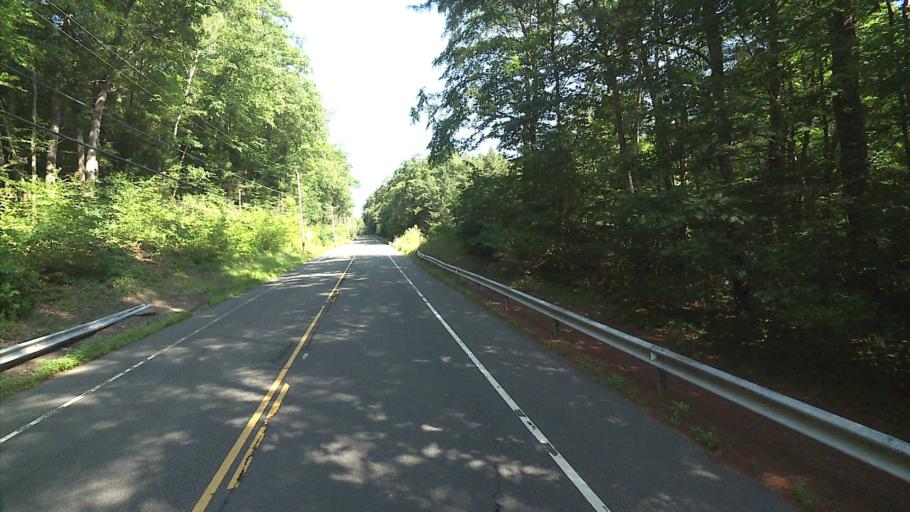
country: US
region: Connecticut
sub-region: Hartford County
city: North Granby
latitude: 41.9630
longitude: -72.8583
